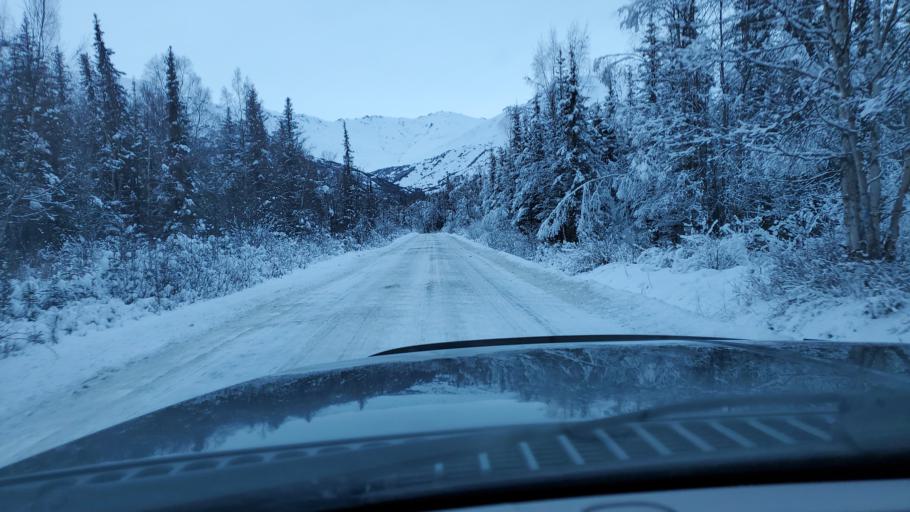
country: US
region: Alaska
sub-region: Matanuska-Susitna Borough
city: Lakes
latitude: 61.6941
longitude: -149.3225
